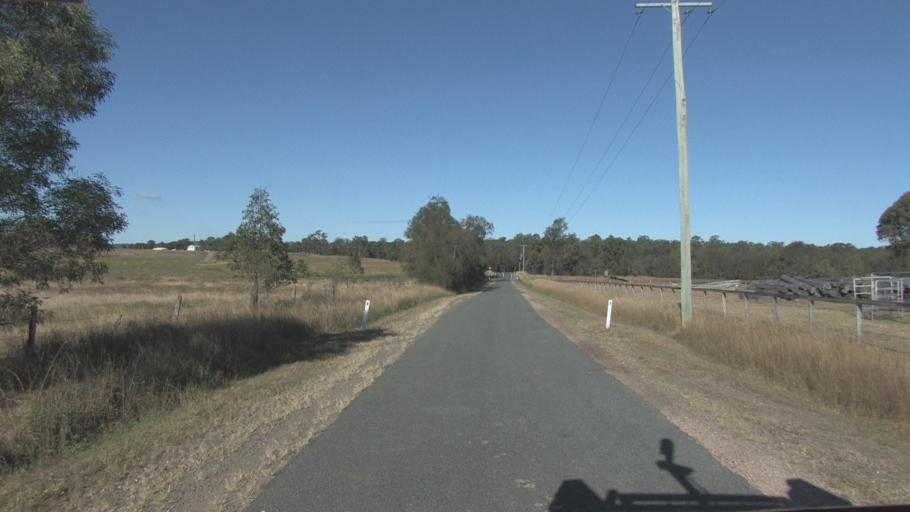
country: AU
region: Queensland
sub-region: Logan
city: Chambers Flat
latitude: -27.7704
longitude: 153.0684
